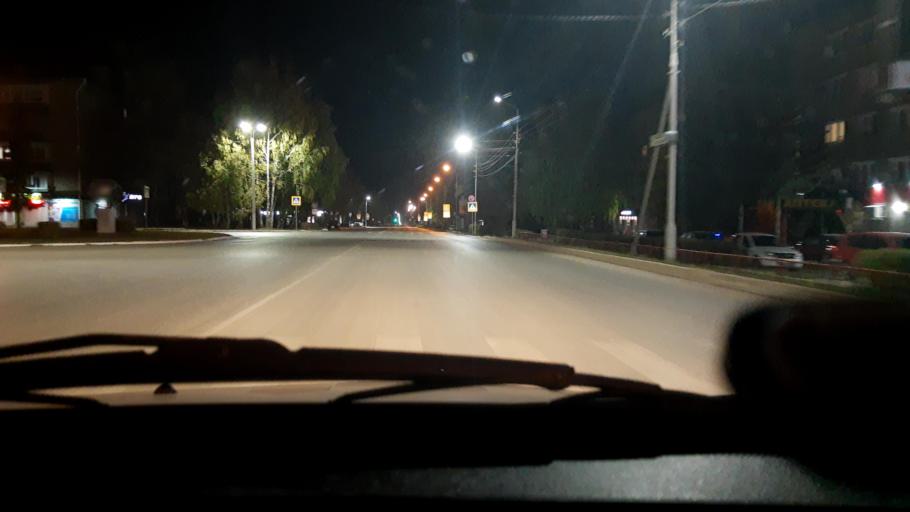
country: RU
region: Bashkortostan
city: Belebey
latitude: 54.0995
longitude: 54.1057
